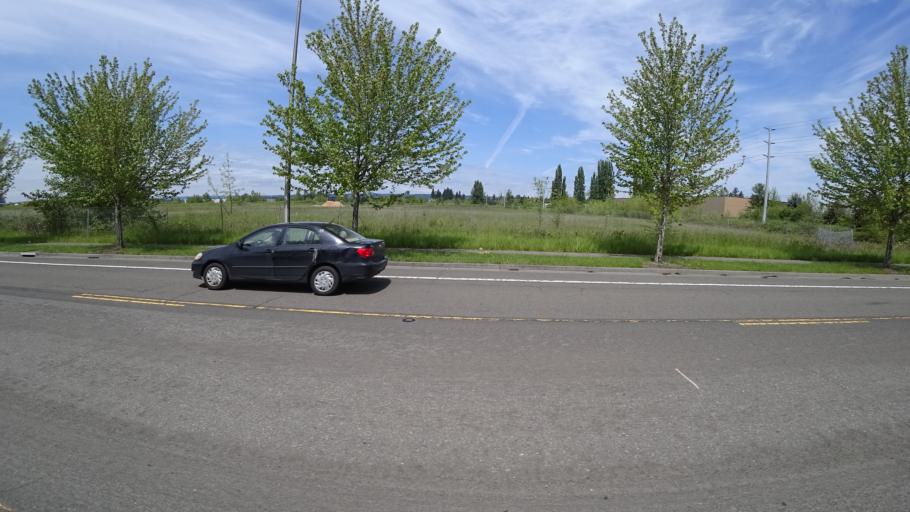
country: US
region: Oregon
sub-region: Washington County
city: Rockcreek
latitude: 45.5650
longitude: -122.9001
